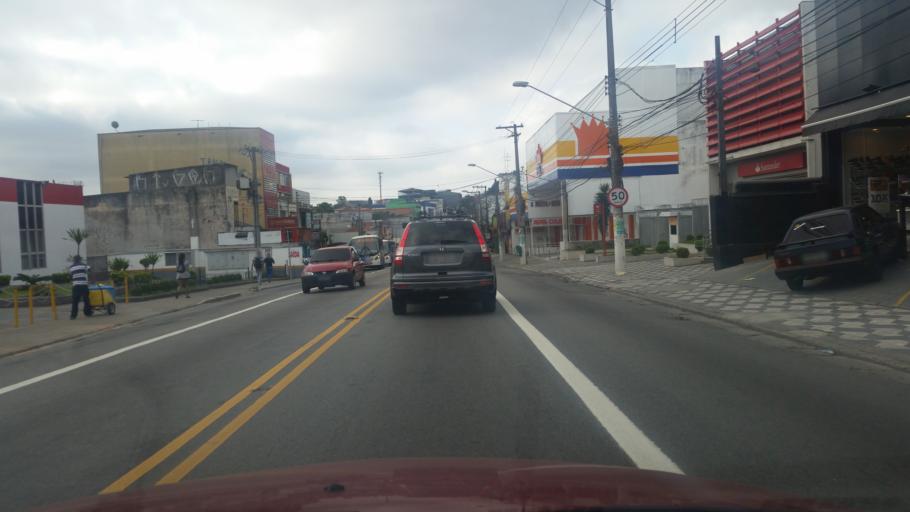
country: BR
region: Sao Paulo
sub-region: Diadema
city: Diadema
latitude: -23.7117
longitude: -46.6990
